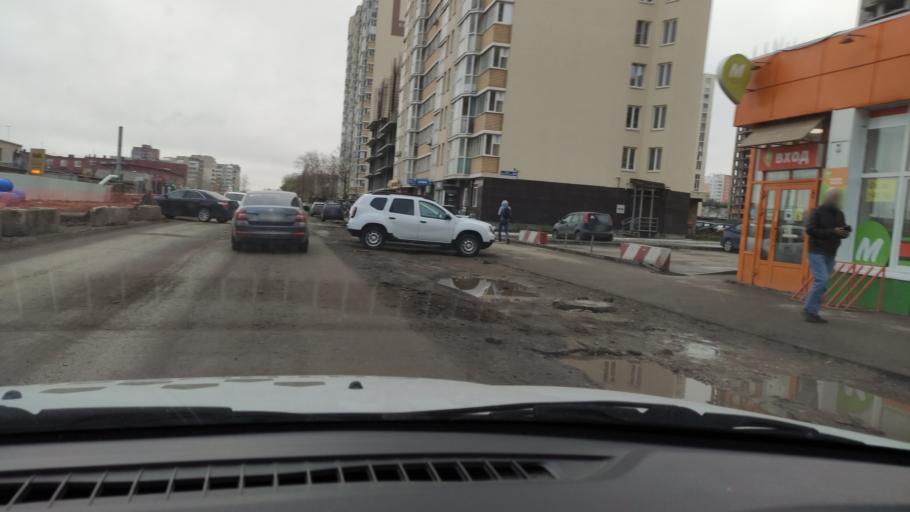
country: RU
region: Perm
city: Perm
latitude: 57.9693
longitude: 56.2034
